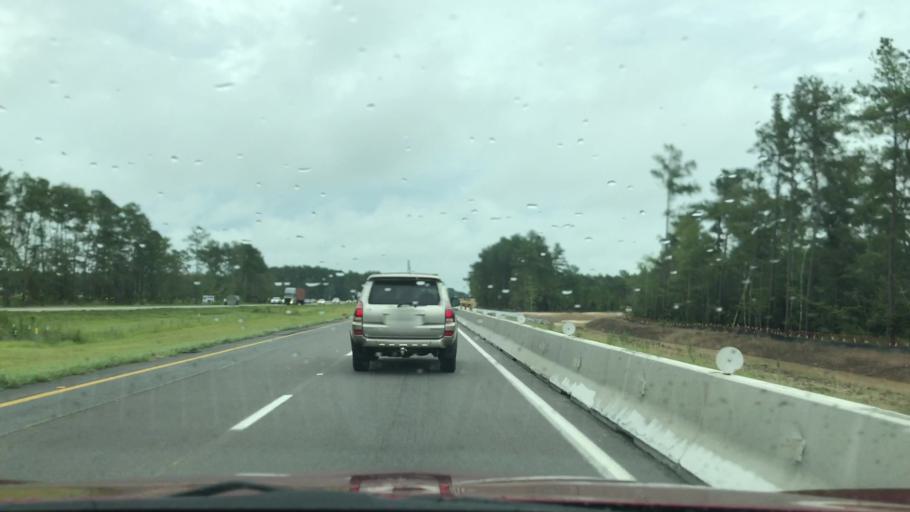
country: US
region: South Carolina
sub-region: Dorchester County
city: Ridgeville
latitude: 33.1235
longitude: -80.2826
